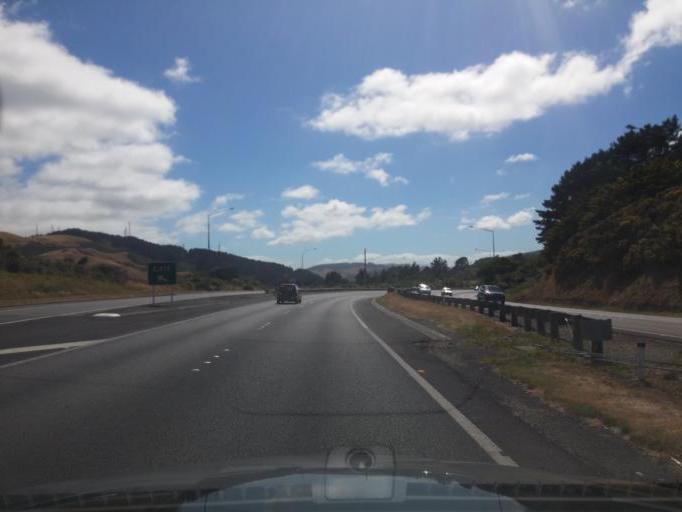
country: NZ
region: Wellington
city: Petone
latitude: -41.2071
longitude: 174.8174
